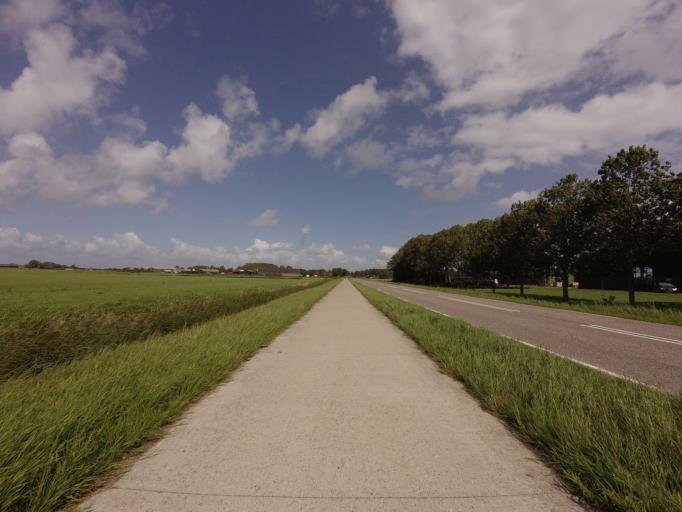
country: NL
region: Friesland
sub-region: Gemeente Harlingen
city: Harlingen
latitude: 53.1443
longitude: 5.4779
